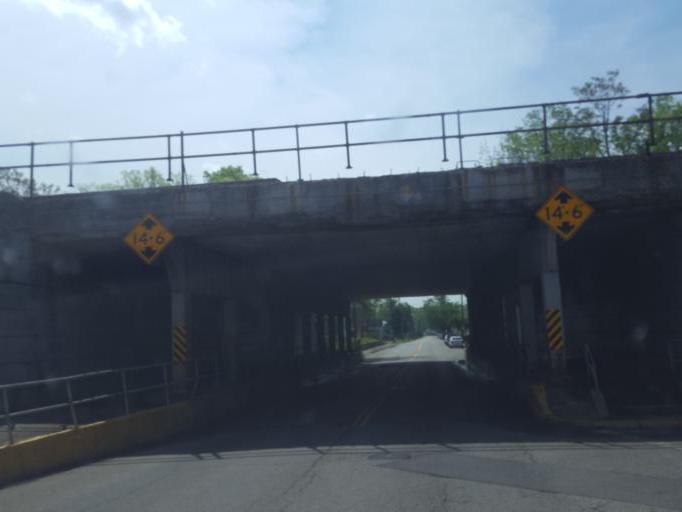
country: US
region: Ohio
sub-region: Licking County
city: Newark
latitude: 40.0547
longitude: -82.4031
